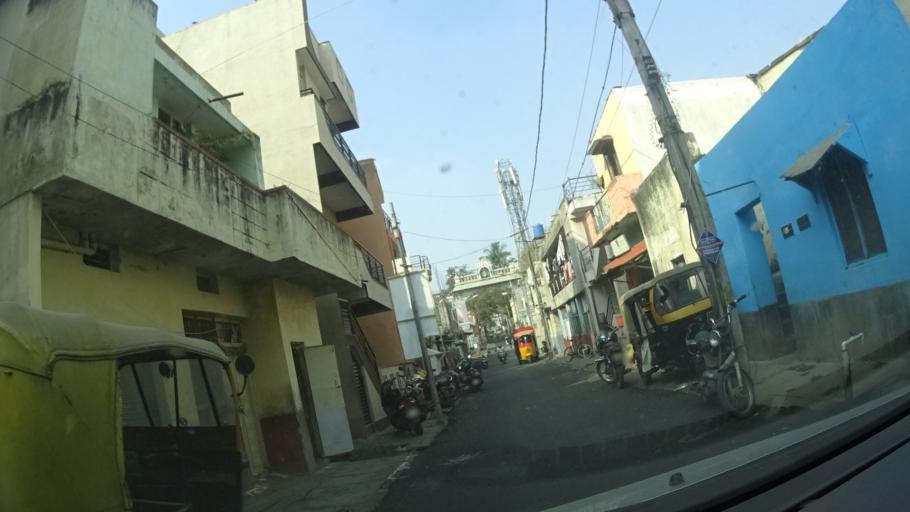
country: IN
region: Karnataka
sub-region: Bangalore Urban
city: Bangalore
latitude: 12.9507
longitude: 77.5644
